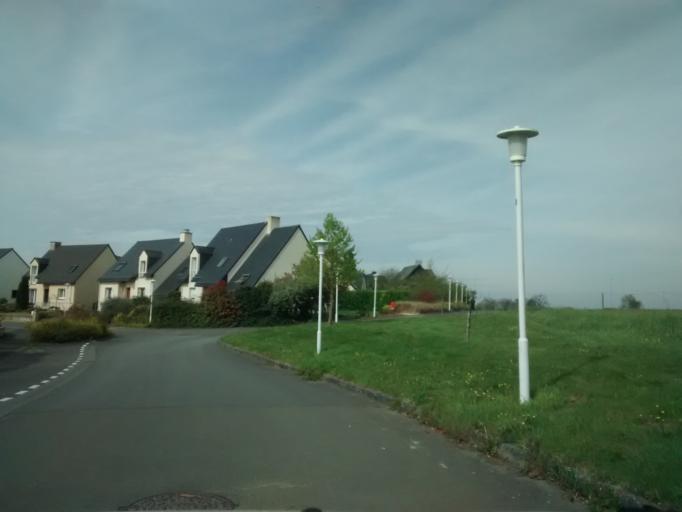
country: FR
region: Brittany
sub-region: Departement d'Ille-et-Vilaine
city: Noyal-sur-Vilaine
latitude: 48.1229
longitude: -1.5258
